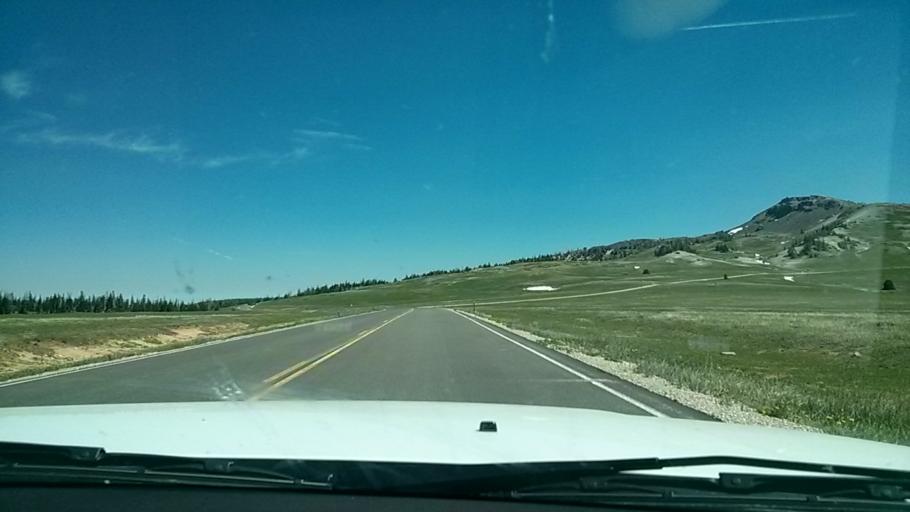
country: US
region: Utah
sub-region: Iron County
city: Parowan
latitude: 37.6644
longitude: -112.8380
